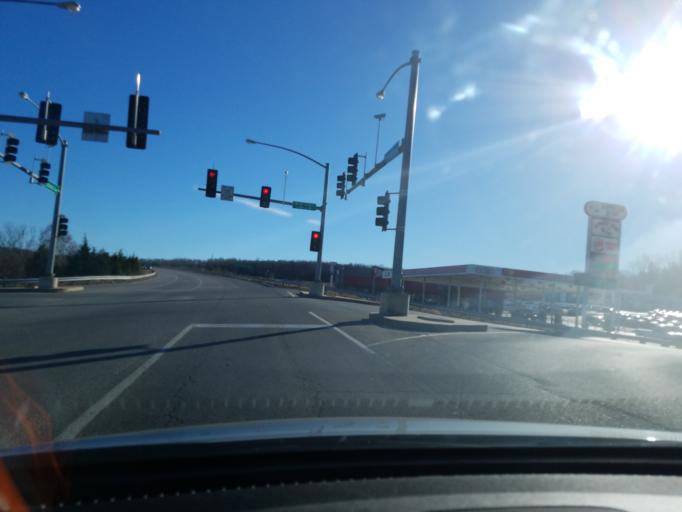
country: US
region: Missouri
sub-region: Pulaski County
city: Waynesville
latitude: 37.8081
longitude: -92.2235
